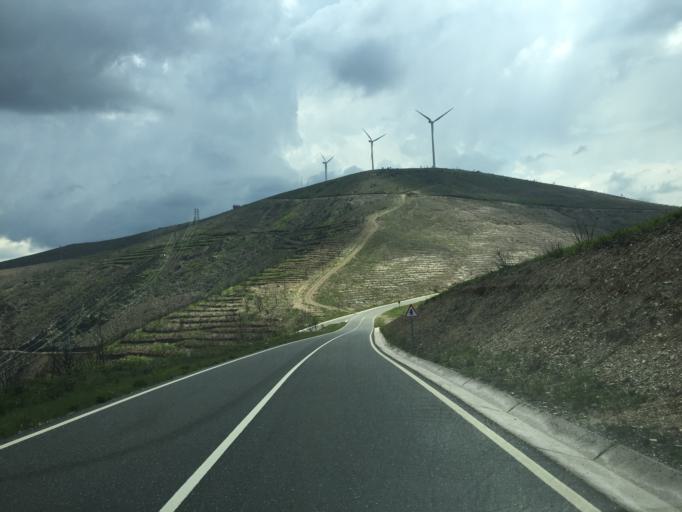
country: PT
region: Coimbra
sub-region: Pampilhosa da Serra
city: Pampilhosa da Serra
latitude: 40.1381
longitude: -7.9062
